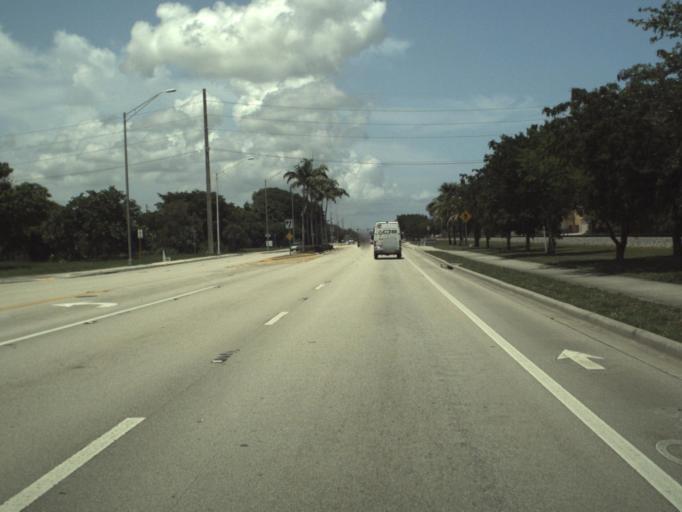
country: US
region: Florida
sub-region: Broward County
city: Deerfield Beach
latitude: 26.3077
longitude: -80.1044
